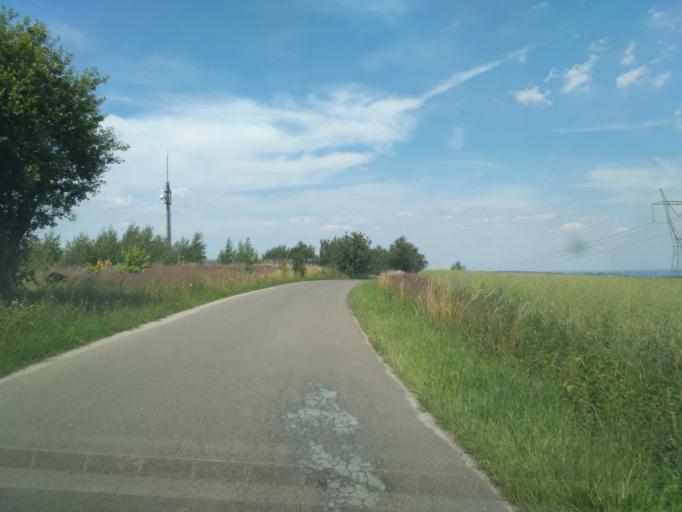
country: PL
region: Subcarpathian Voivodeship
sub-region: Powiat strzyzowski
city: Jawornik
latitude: 49.8707
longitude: 21.8579
